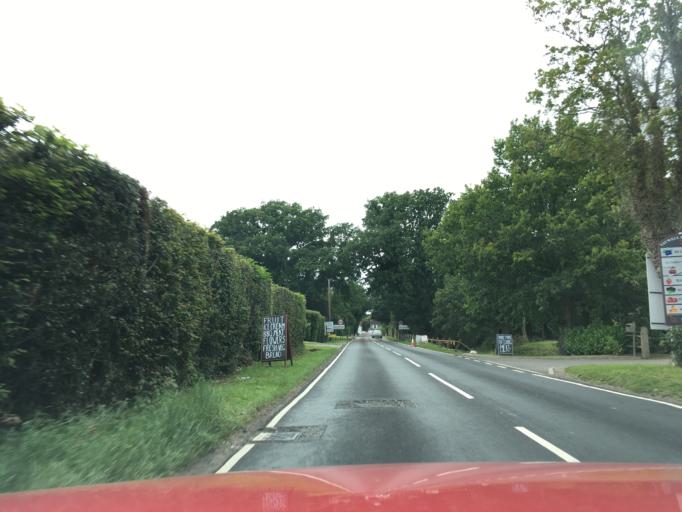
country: GB
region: England
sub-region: Kent
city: Cranbrook
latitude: 51.1134
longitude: 0.4762
